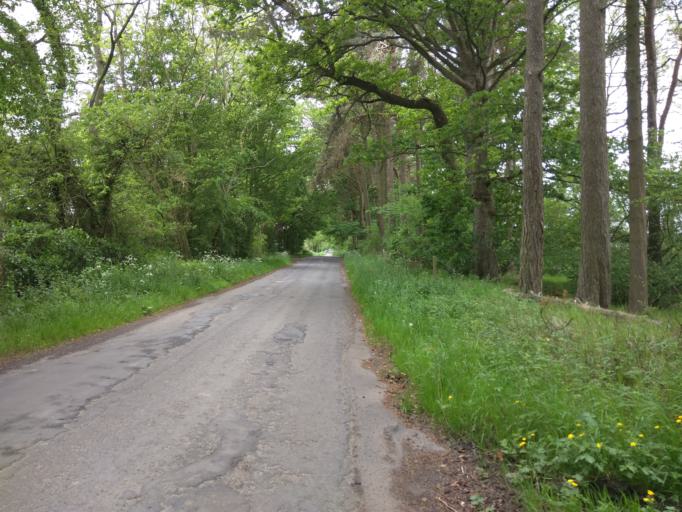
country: GB
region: Scotland
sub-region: Edinburgh
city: Balerno
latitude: 55.8750
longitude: -3.3565
